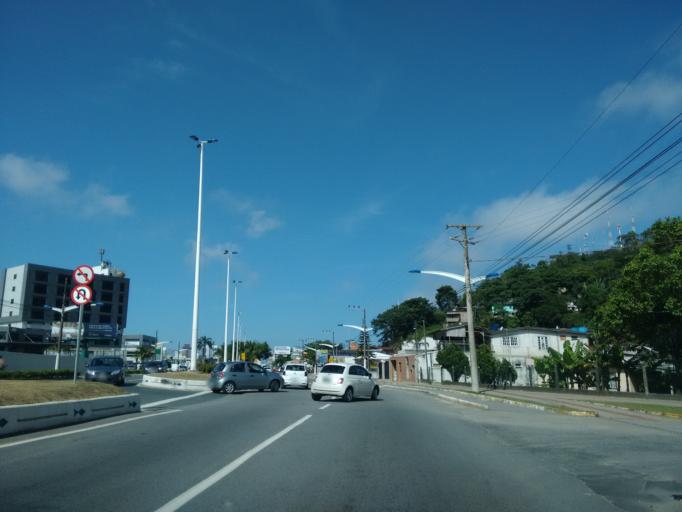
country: BR
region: Santa Catarina
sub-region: Itajai
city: Itajai
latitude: -26.9201
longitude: -48.6711
